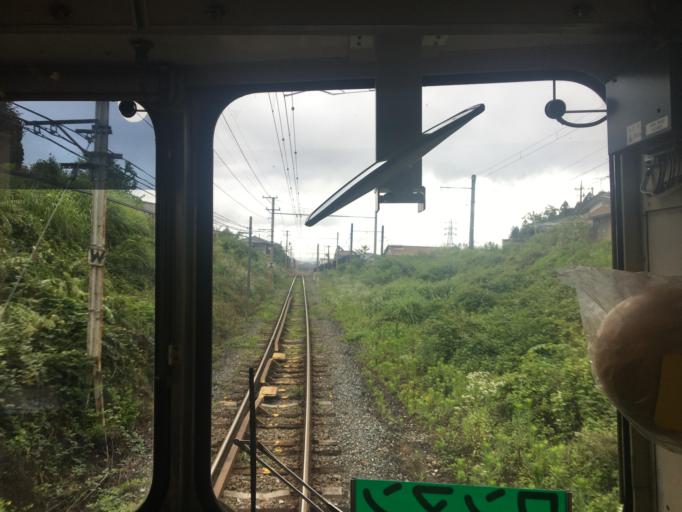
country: JP
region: Saitama
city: Chichibu
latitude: 35.9676
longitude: 139.0650
